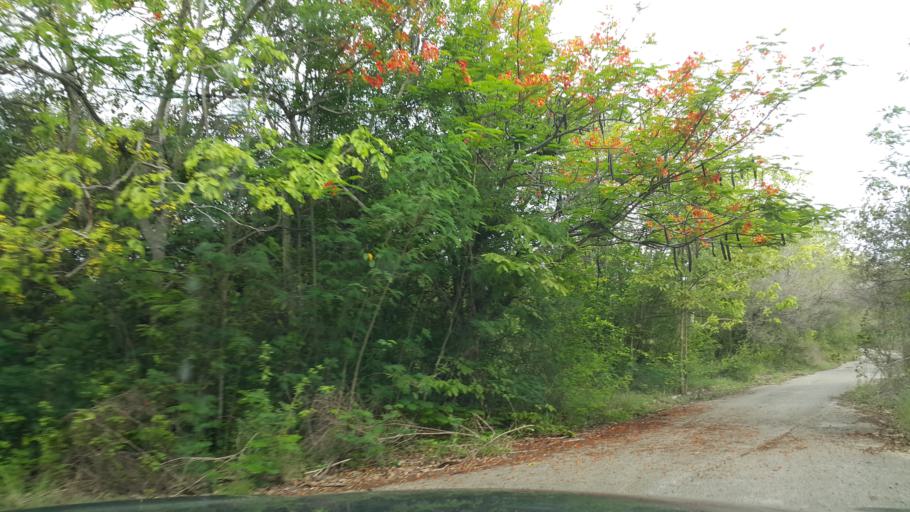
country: TH
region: Chiang Mai
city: San Kamphaeng
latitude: 18.7583
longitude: 99.1183
